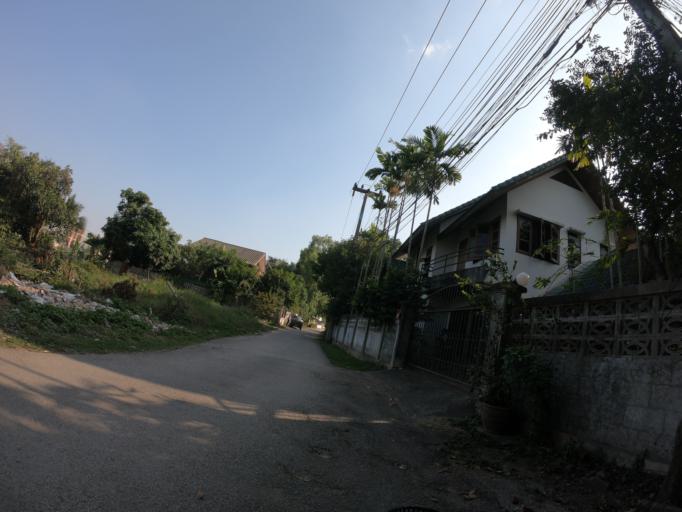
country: TH
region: Chiang Mai
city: Chiang Mai
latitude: 18.8350
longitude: 98.9853
